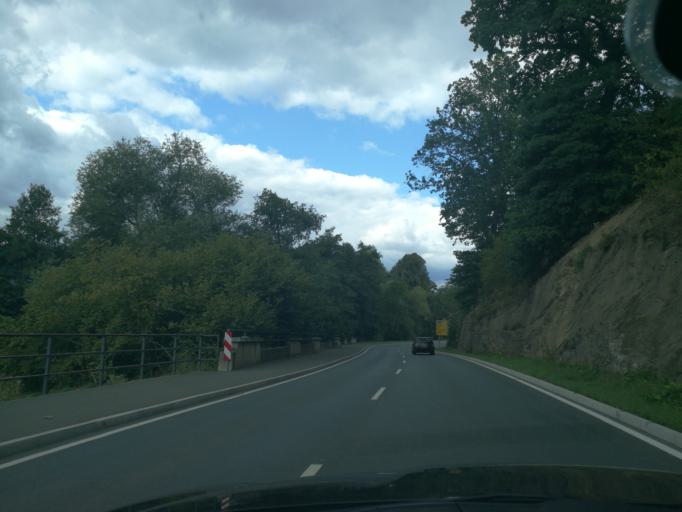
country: DE
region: Saxony
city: Oelsnitz
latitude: 50.3996
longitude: 12.1861
